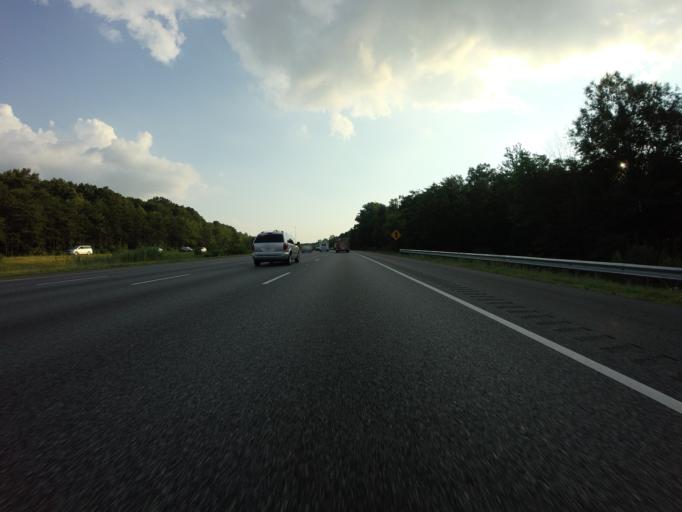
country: US
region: Maryland
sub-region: Howard County
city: North Laurel
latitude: 39.1324
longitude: -76.8590
